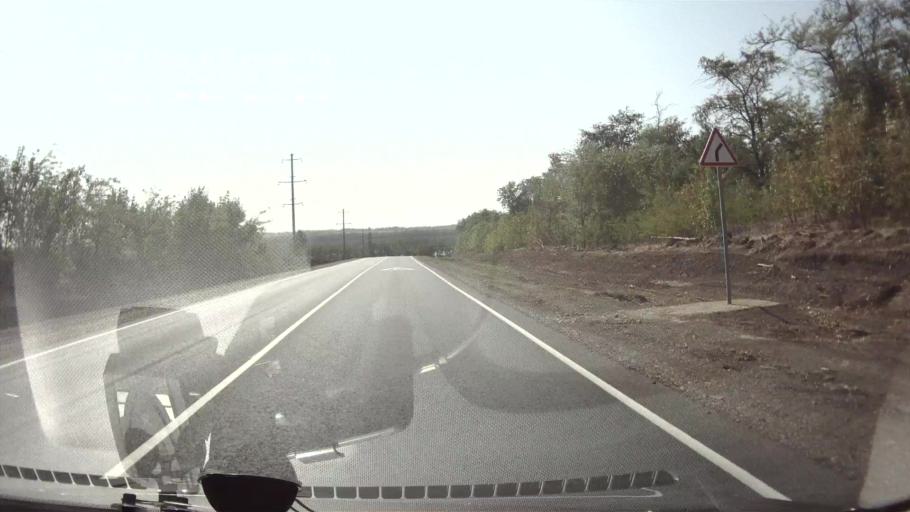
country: RU
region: Krasnodarskiy
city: Kavkazskaya
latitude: 45.5543
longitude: 40.6930
